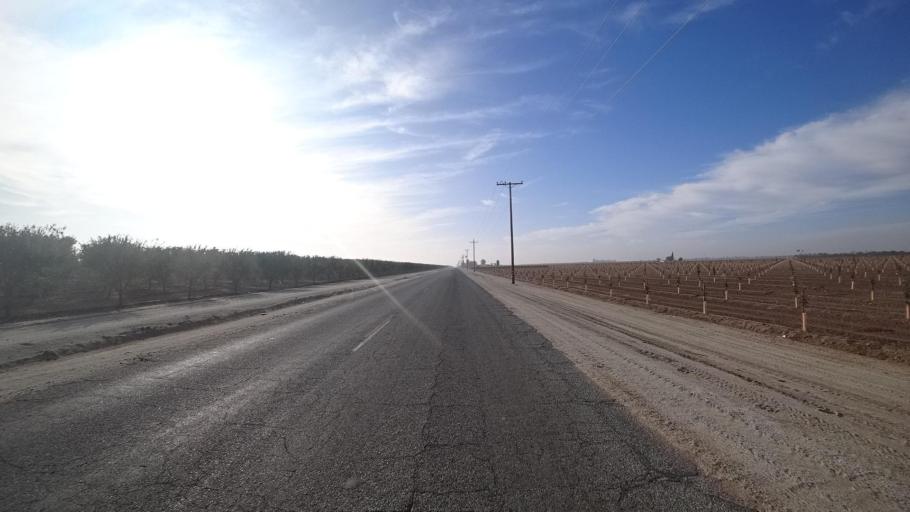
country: US
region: California
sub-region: Kern County
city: McFarland
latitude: 35.6946
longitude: -119.2049
